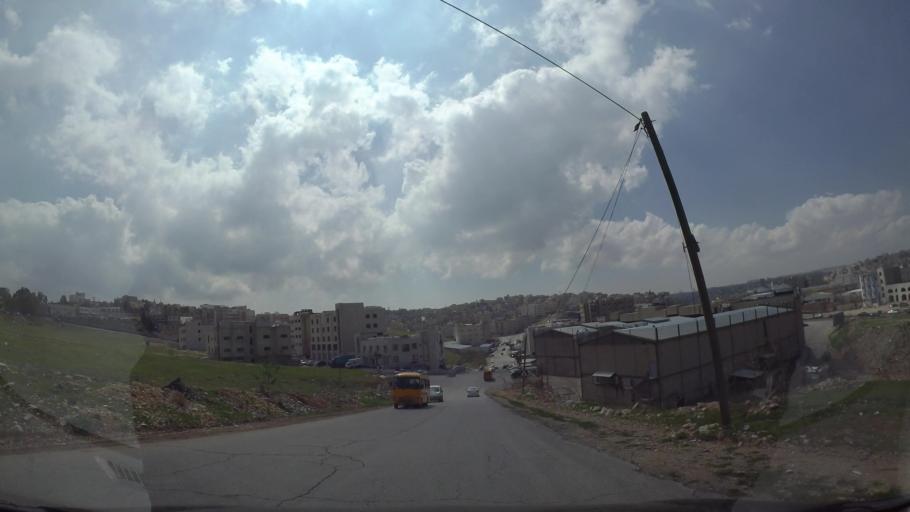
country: JO
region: Zarqa
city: Russeifa
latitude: 31.9958
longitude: 35.9958
